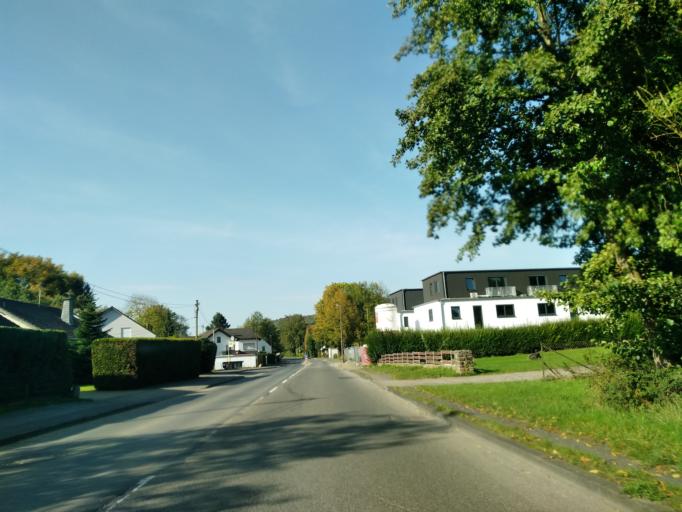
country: DE
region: North Rhine-Westphalia
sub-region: Regierungsbezirk Koln
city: Hennef
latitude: 50.7273
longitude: 7.2705
